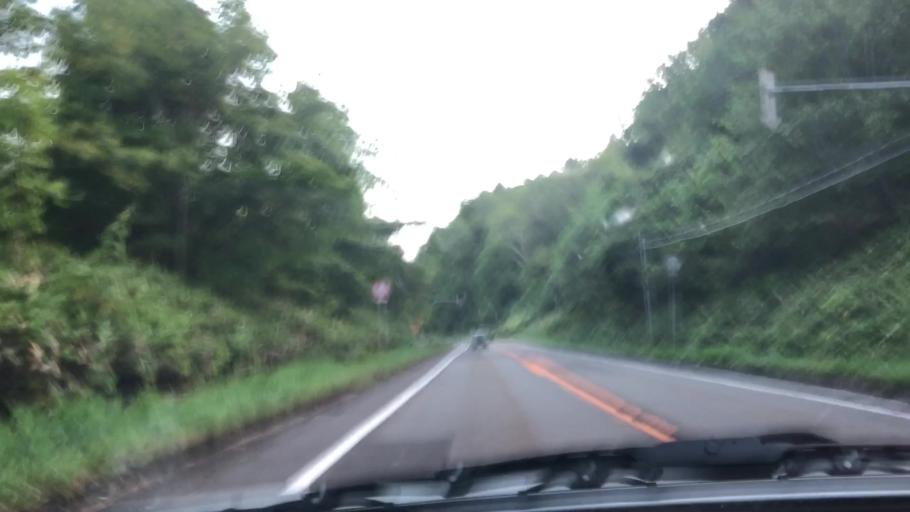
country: JP
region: Hokkaido
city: Shimo-furano
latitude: 42.8839
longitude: 142.2329
